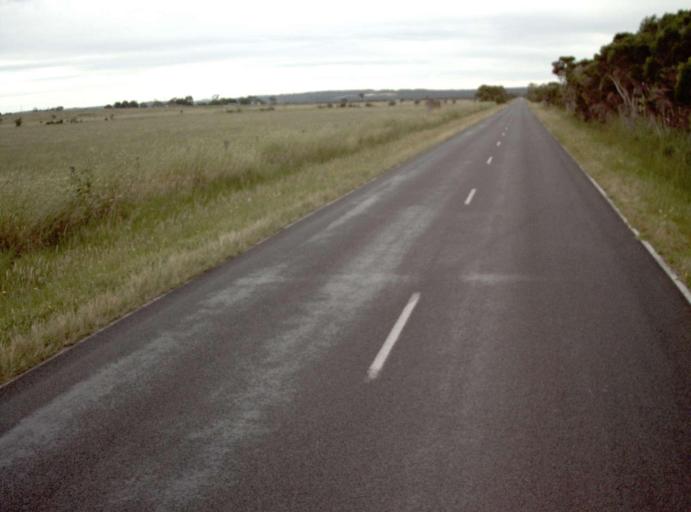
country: AU
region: Victoria
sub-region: Bass Coast
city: Cowes
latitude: -38.4249
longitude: 145.4507
